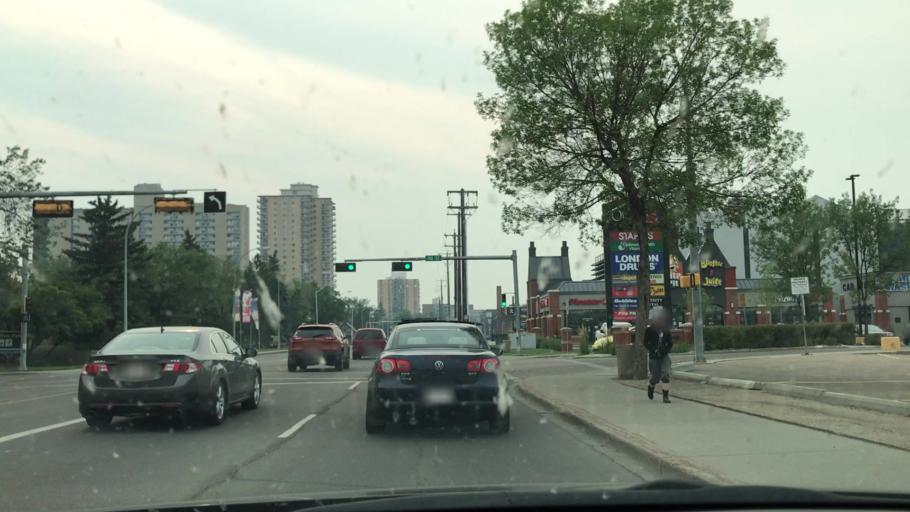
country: CA
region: Alberta
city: Edmonton
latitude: 53.5463
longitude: -113.5244
